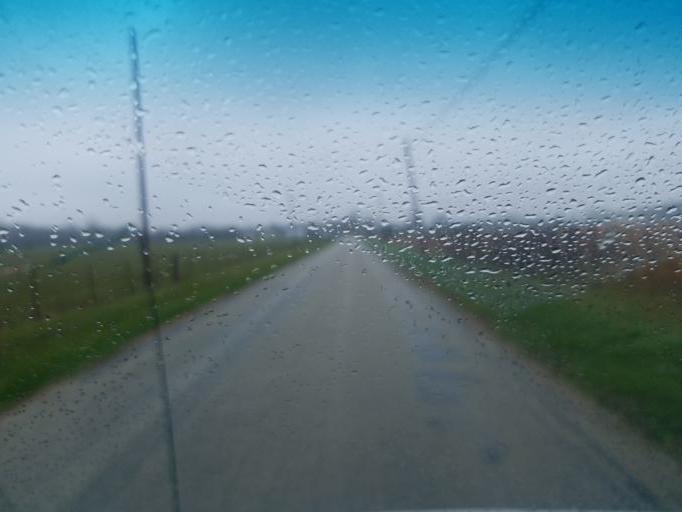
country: US
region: Ohio
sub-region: Wood County
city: North Baltimore
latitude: 41.2222
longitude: -83.6403
